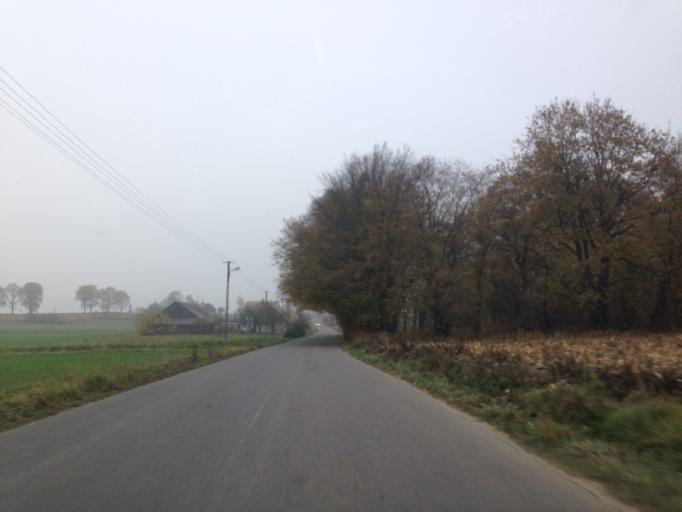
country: PL
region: Warmian-Masurian Voivodeship
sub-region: Powiat nowomiejski
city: Biskupiec
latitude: 53.5340
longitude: 19.4602
